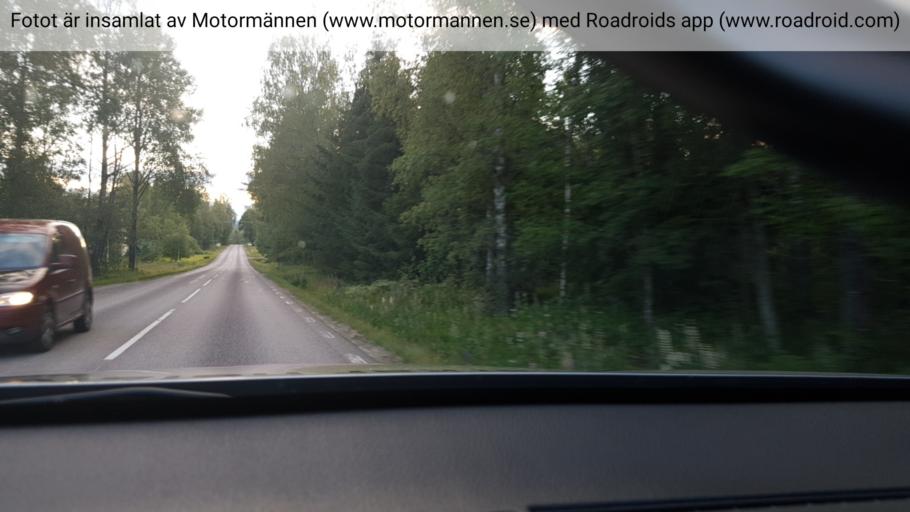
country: SE
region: Vaermland
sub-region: Torsby Kommun
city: Torsby
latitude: 60.1328
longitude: 13.0471
